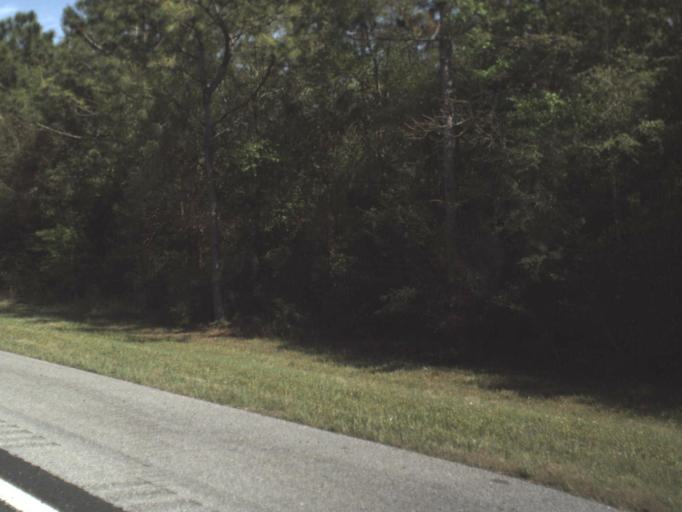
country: US
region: Florida
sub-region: Okaloosa County
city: Crestview
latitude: 30.7098
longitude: -86.7126
